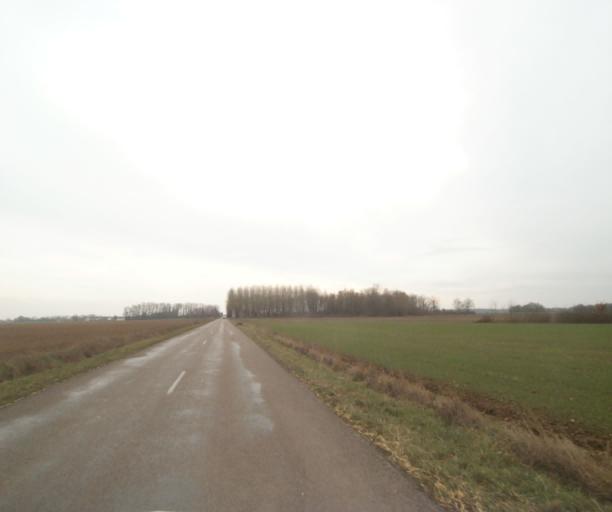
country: FR
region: Champagne-Ardenne
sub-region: Departement de la Haute-Marne
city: Villiers-en-Lieu
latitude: 48.6765
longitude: 4.8876
